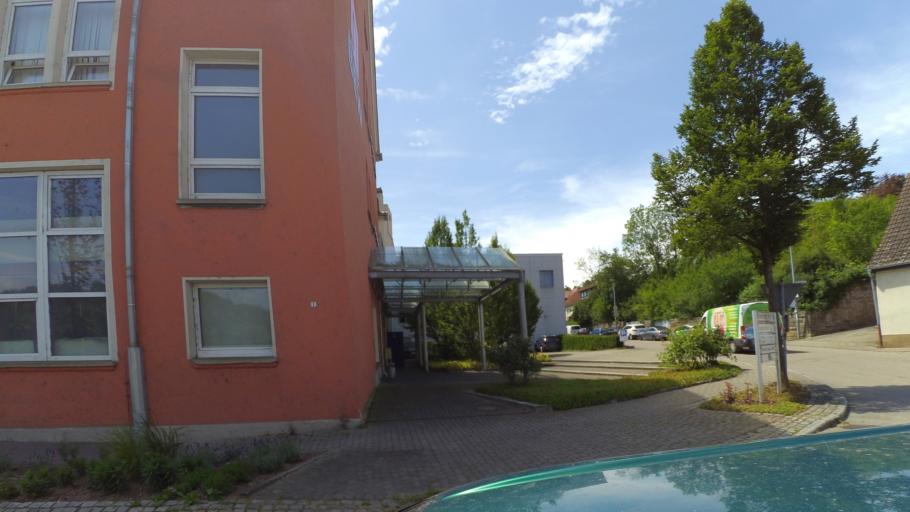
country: DE
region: Baden-Wuerttemberg
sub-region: Regierungsbezirk Stuttgart
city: Michelbach an der Bilz
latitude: 49.0518
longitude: 9.7384
